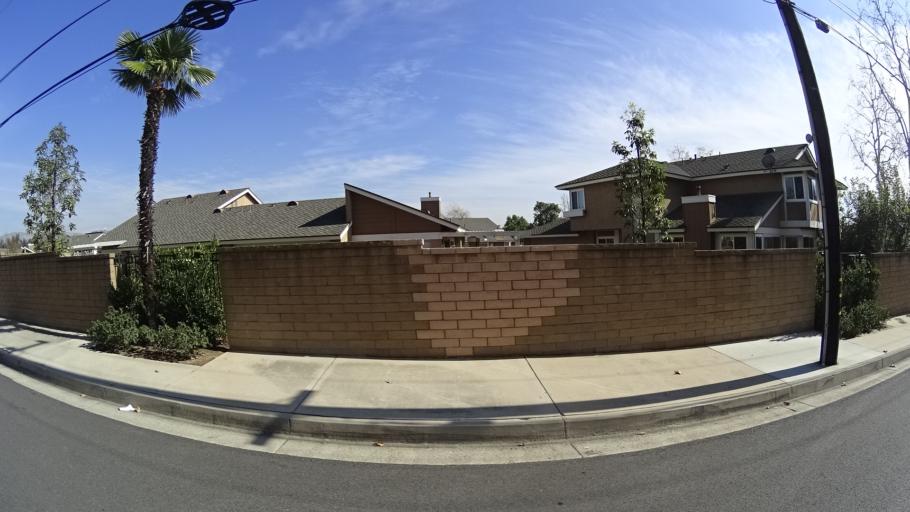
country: US
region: California
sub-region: Orange County
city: Placentia
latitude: 33.9045
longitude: -117.8637
